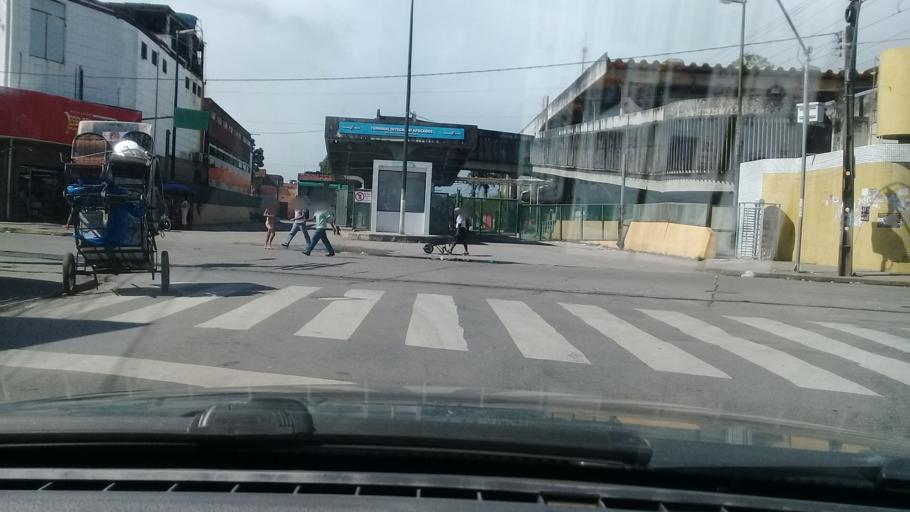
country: BR
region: Pernambuco
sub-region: Recife
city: Recife
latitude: -8.0775
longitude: -34.9072
